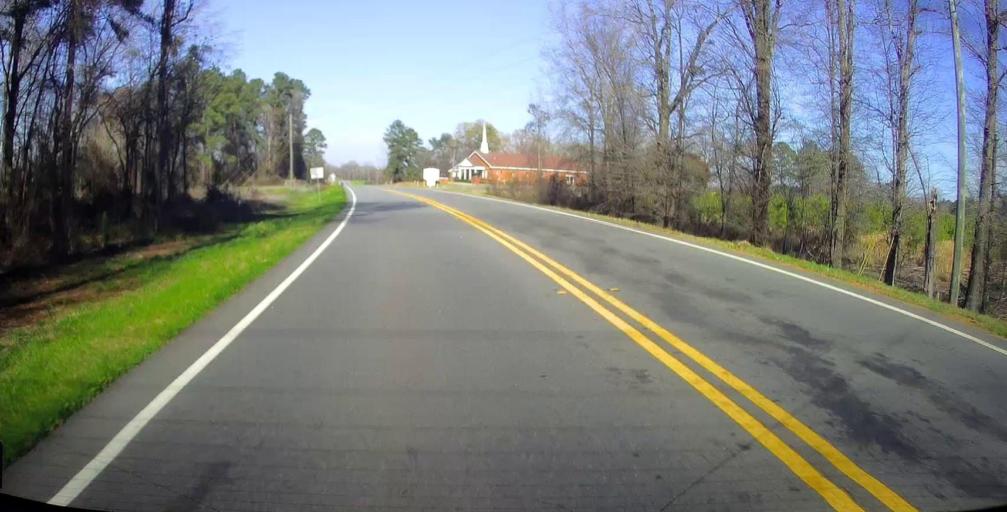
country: US
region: Georgia
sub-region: Macon County
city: Montezuma
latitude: 32.2929
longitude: -83.9161
